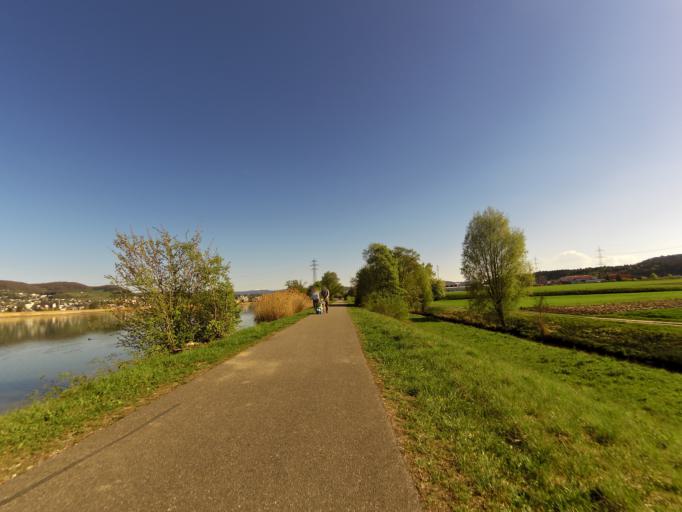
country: CH
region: Aargau
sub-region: Bezirk Zurzach
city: Klingnau
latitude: 47.5824
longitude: 8.2339
